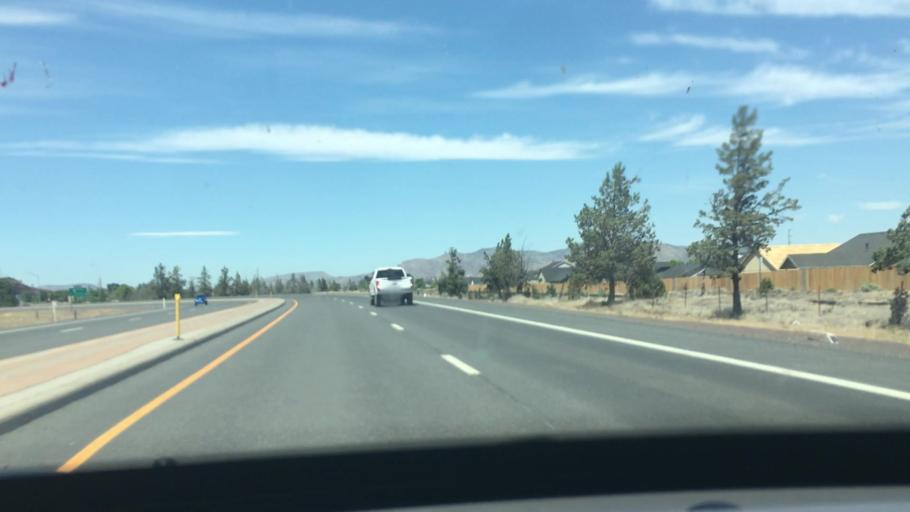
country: US
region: Oregon
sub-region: Deschutes County
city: Redmond
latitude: 44.2953
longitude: -121.1664
